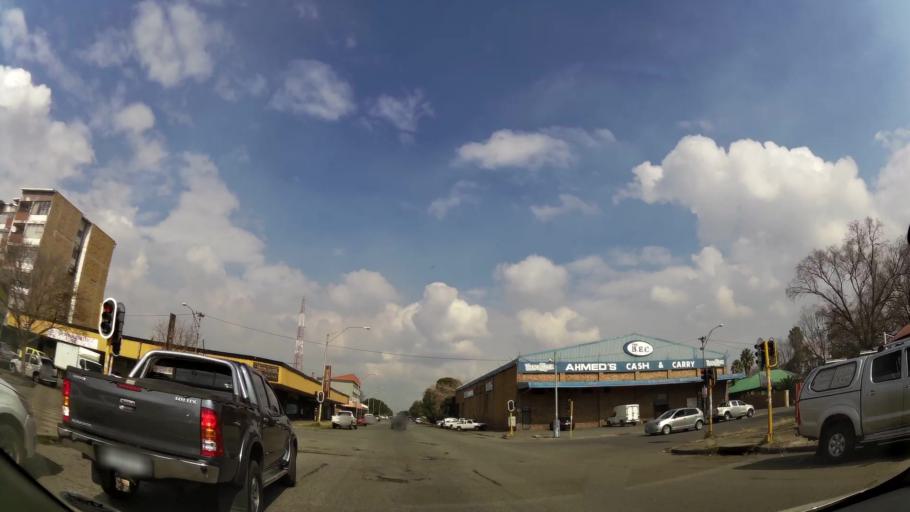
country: ZA
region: Gauteng
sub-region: Sedibeng District Municipality
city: Vereeniging
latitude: -26.6773
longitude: 27.9288
